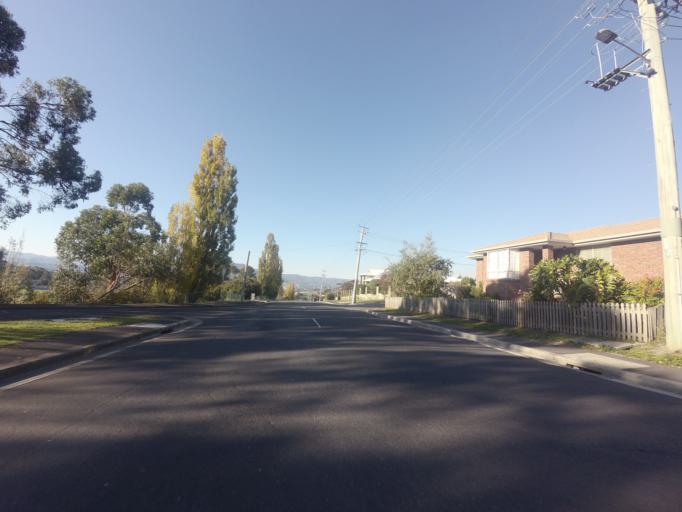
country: AU
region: Tasmania
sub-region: Glenorchy
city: West Moonah
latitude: -42.8506
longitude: 147.2567
